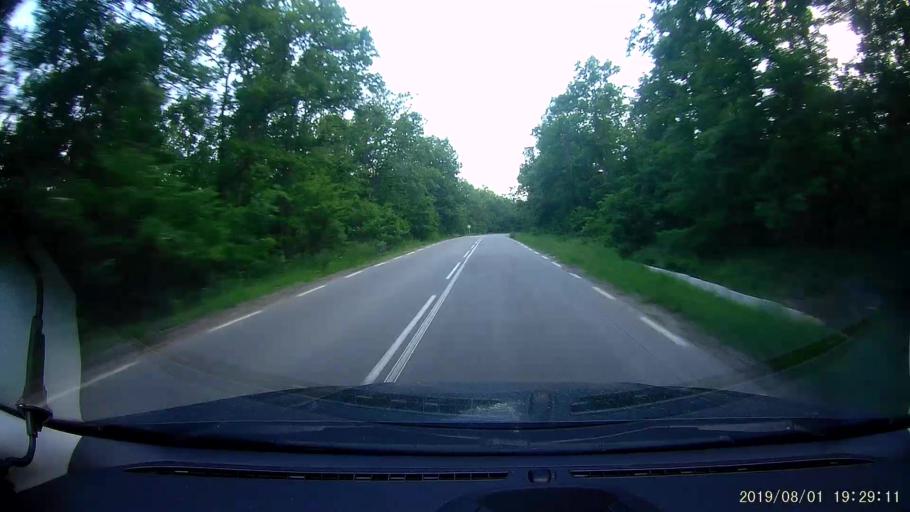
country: BG
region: Burgas
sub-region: Obshtina Sungurlare
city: Sungurlare
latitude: 42.8302
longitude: 26.9099
